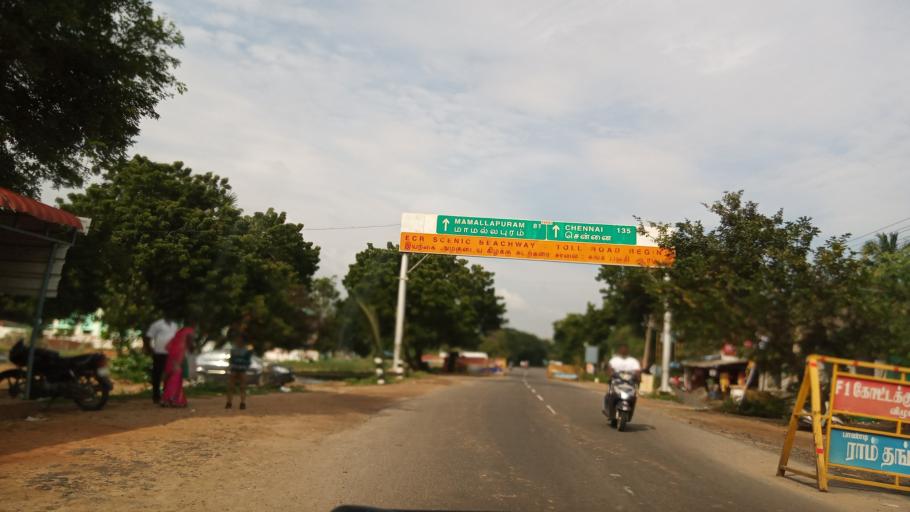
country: IN
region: Tamil Nadu
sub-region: Villupuram
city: Auroville
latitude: 12.0563
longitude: 79.8741
